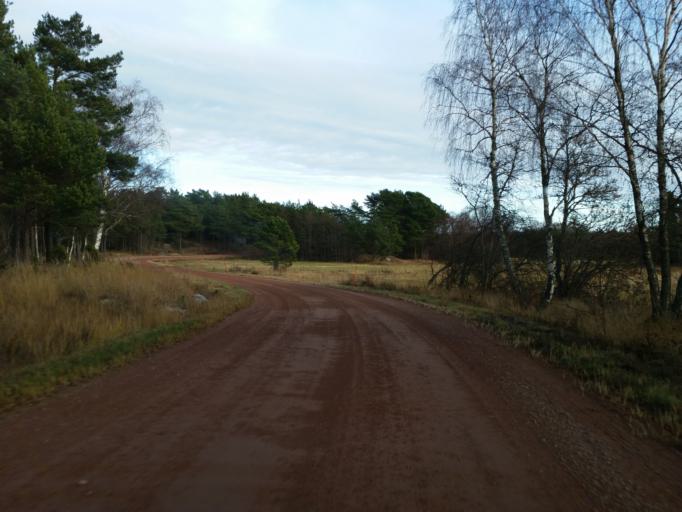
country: AX
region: Alands skaergard
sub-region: Kumlinge
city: Kumlinge
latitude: 60.2542
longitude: 20.8087
